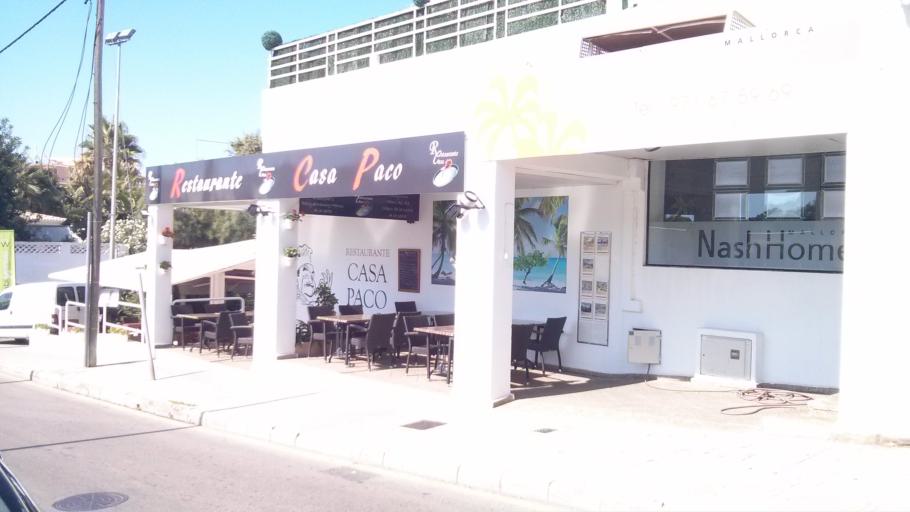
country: ES
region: Balearic Islands
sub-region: Illes Balears
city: Magaluf
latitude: 39.5351
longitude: 2.5718
